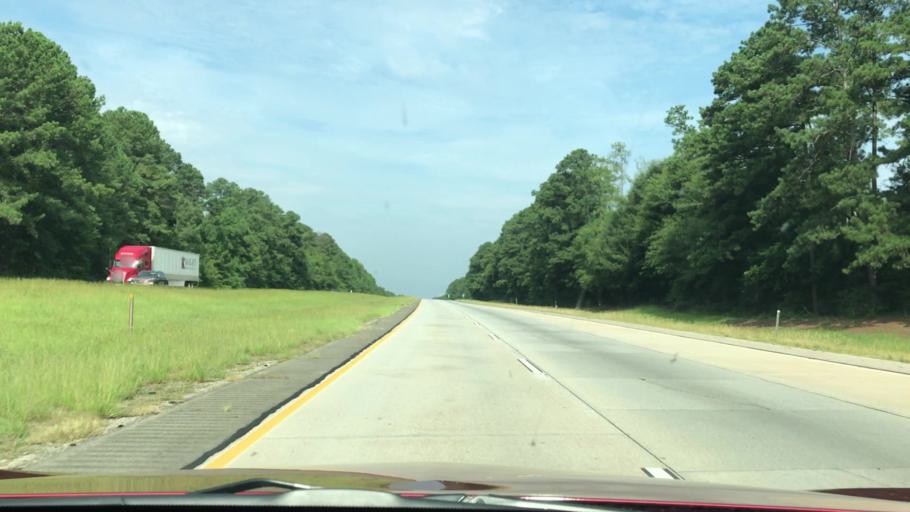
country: US
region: Georgia
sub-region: Warren County
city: Firing Range
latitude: 33.5034
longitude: -82.7195
